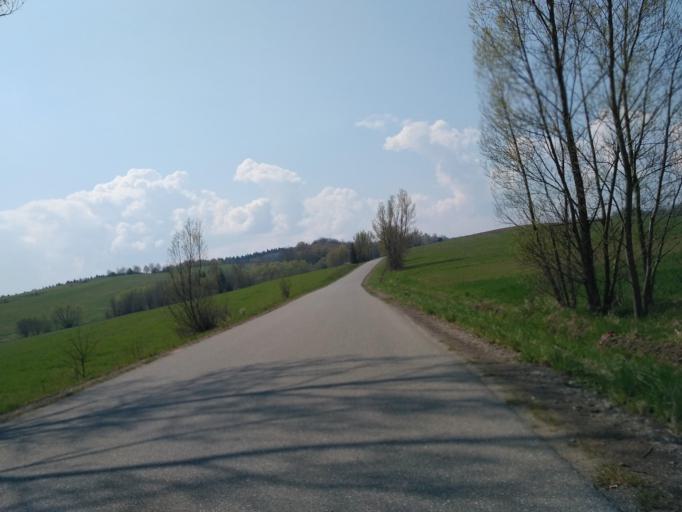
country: PL
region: Subcarpathian Voivodeship
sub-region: Powiat sanocki
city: Zarszyn
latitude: 49.5724
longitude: 22.0065
